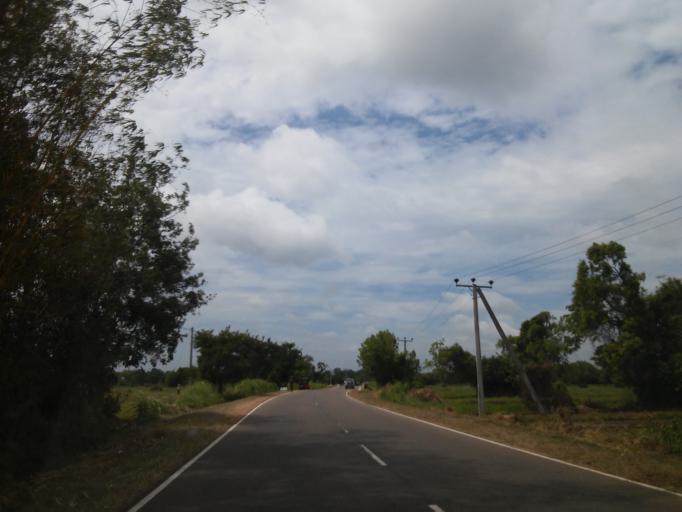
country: LK
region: Central
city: Sigiriya
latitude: 8.0836
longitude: 80.6699
